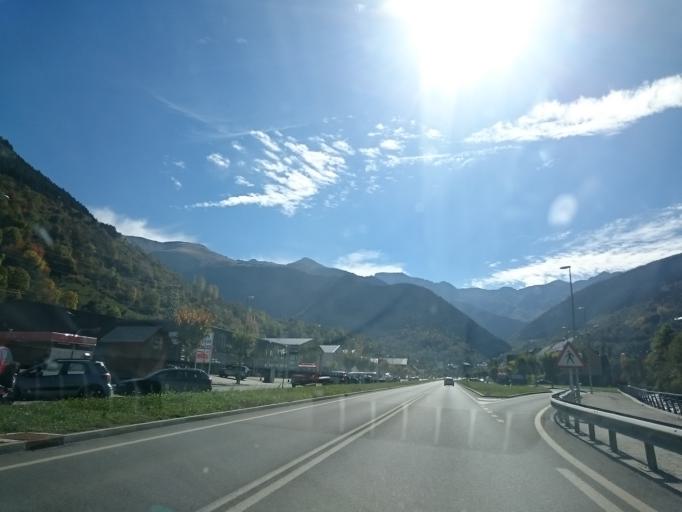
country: ES
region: Catalonia
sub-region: Provincia de Lleida
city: Vielha
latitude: 42.7128
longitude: 0.7971
